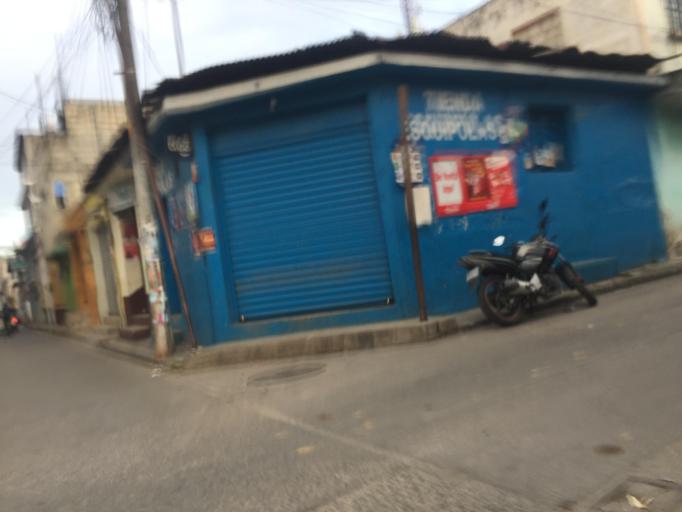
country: GT
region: Totonicapan
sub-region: Municipio de Totonicapan
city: Totonicapan
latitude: 14.9099
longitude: -91.3600
